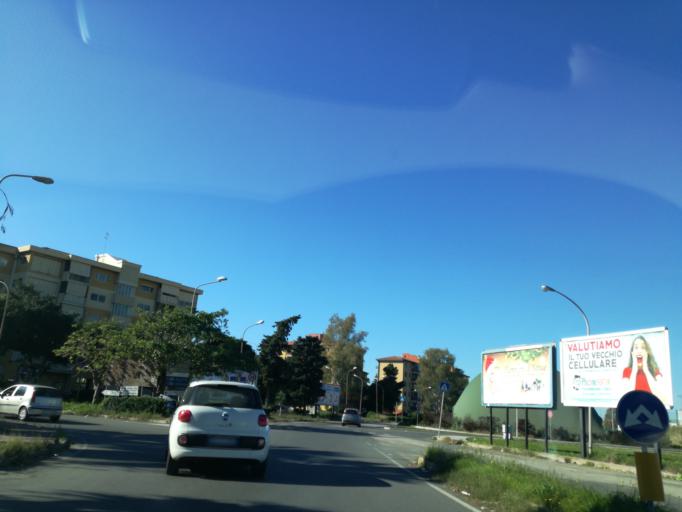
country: IT
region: Sicily
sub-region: Provincia di Caltanissetta
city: Gela
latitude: 37.0800
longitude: 14.2171
